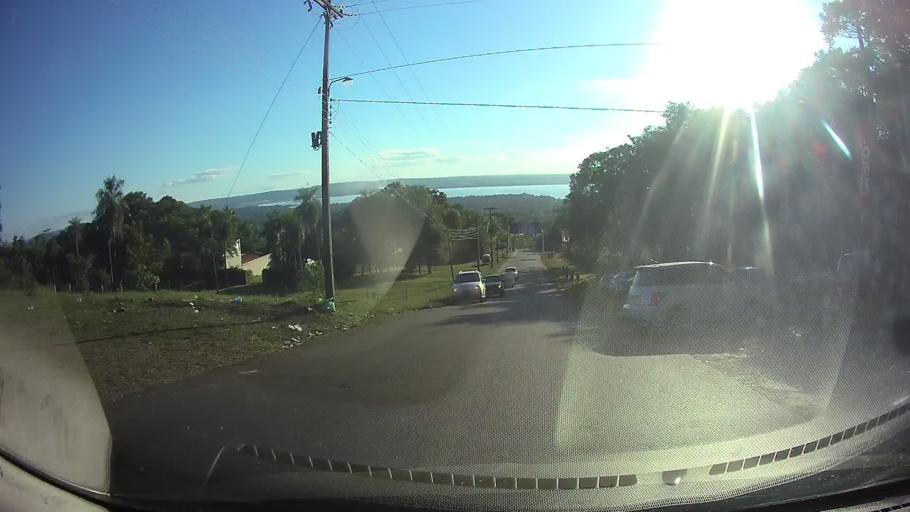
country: PY
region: Cordillera
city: San Bernardino
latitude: -25.3157
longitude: -57.2664
